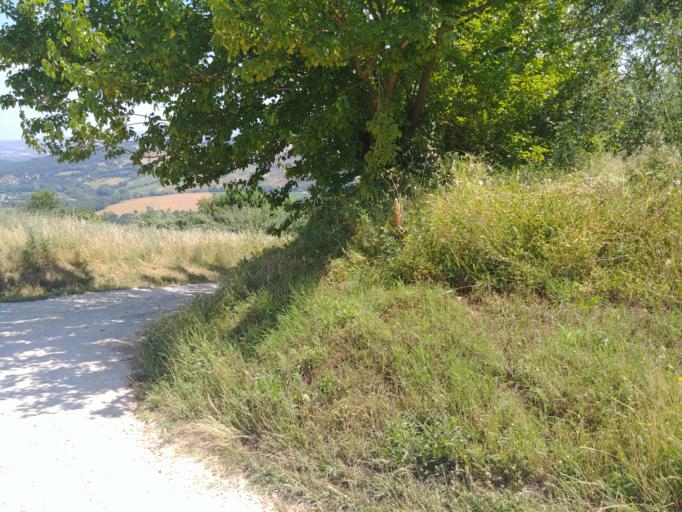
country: IT
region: Umbria
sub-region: Provincia di Perugia
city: Todi
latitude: 42.7579
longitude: 12.3625
